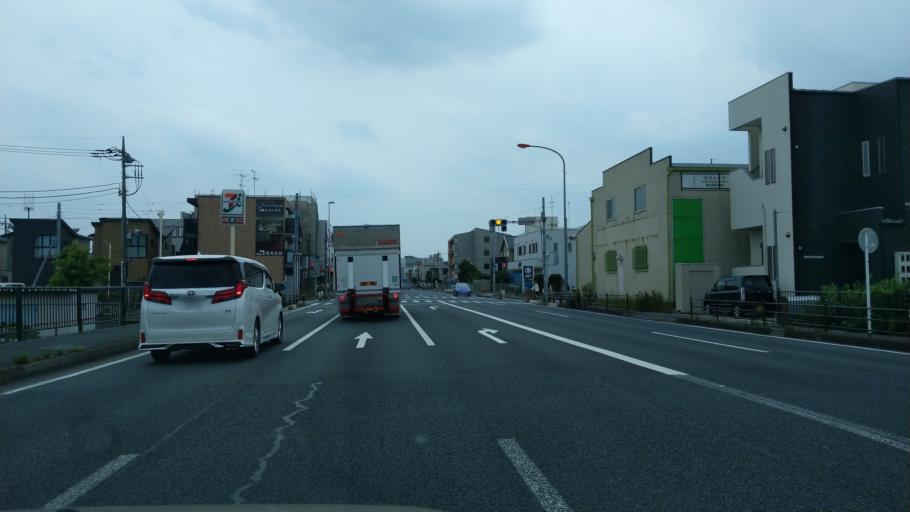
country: JP
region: Saitama
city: Ageoshimo
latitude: 35.9469
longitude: 139.6107
